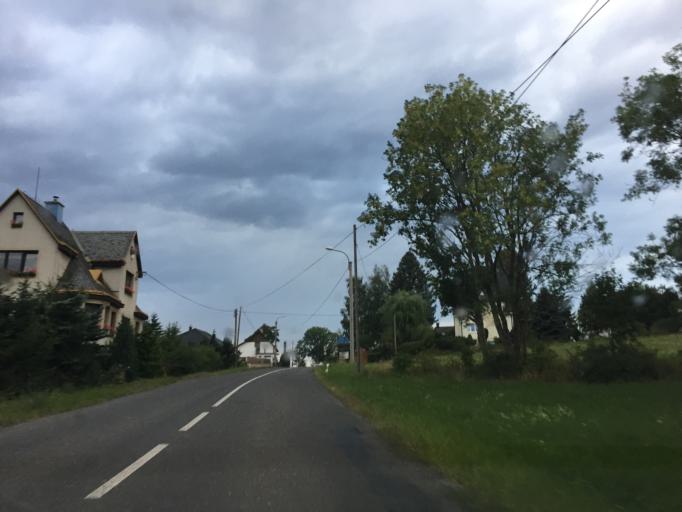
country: CZ
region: Liberecky
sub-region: Okres Jablonec nad Nisou
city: Jablonec nad Nisou
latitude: 50.6963
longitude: 15.1914
